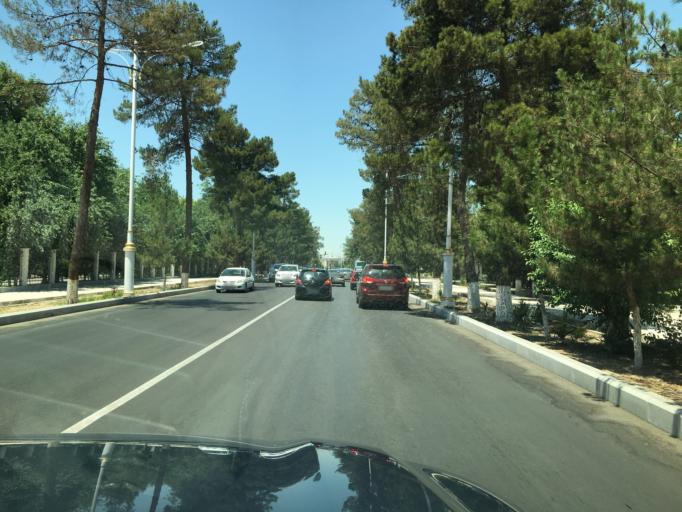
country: TM
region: Ahal
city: Ashgabat
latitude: 37.9371
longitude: 58.3863
